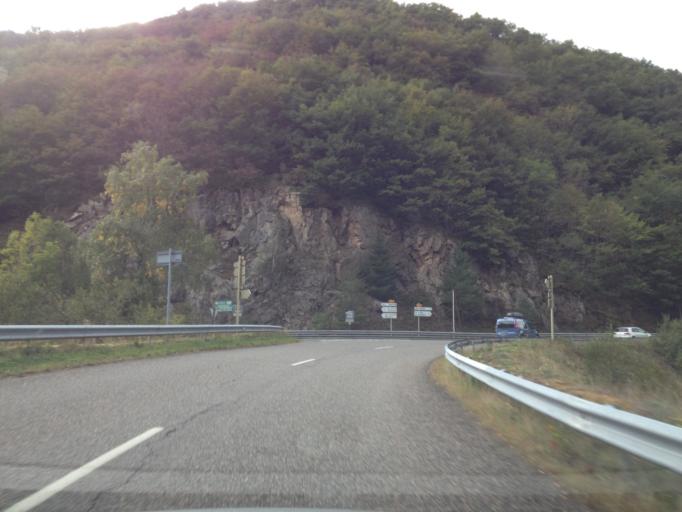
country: FR
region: Rhone-Alpes
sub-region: Departement de la Loire
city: Renaison
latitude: 46.0382
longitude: 3.8681
